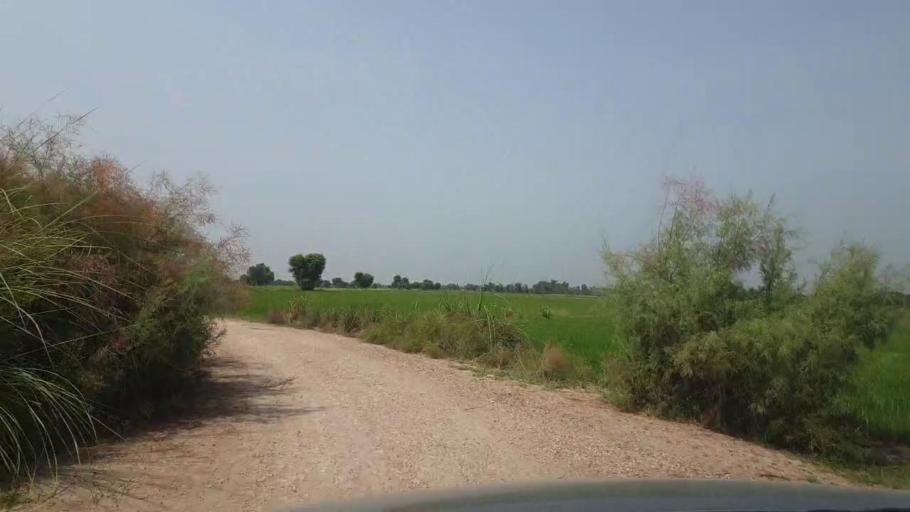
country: PK
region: Sindh
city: Madeji
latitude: 27.7956
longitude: 68.5384
